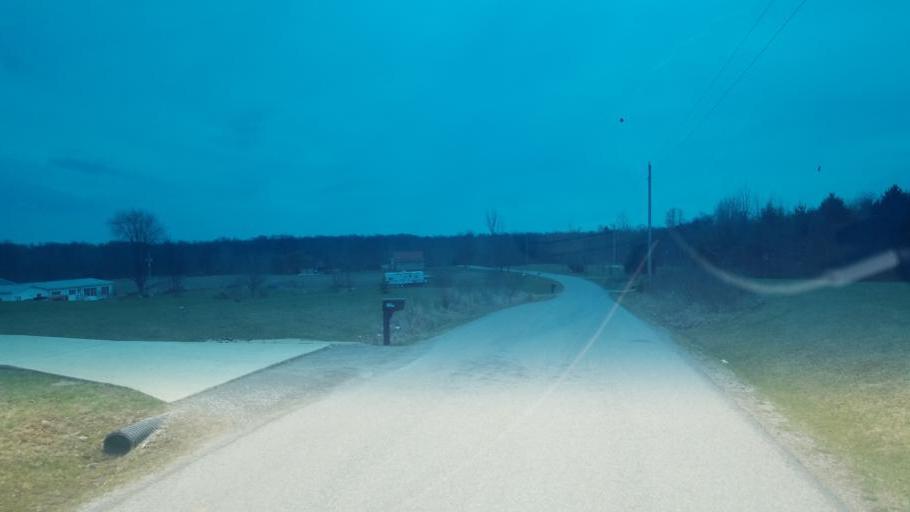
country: US
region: Ohio
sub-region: Knox County
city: Centerburg
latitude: 40.3648
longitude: -82.6583
